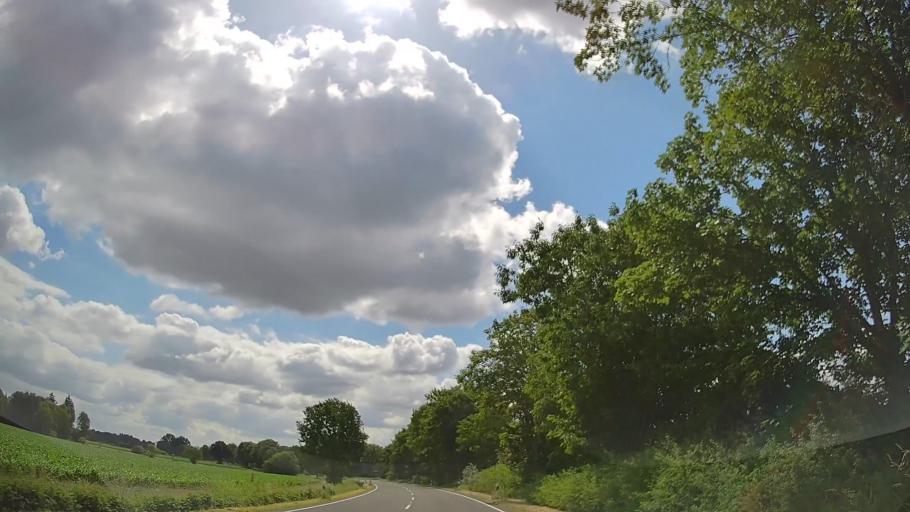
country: DE
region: Lower Saxony
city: Vechta
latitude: 52.6930
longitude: 8.3057
